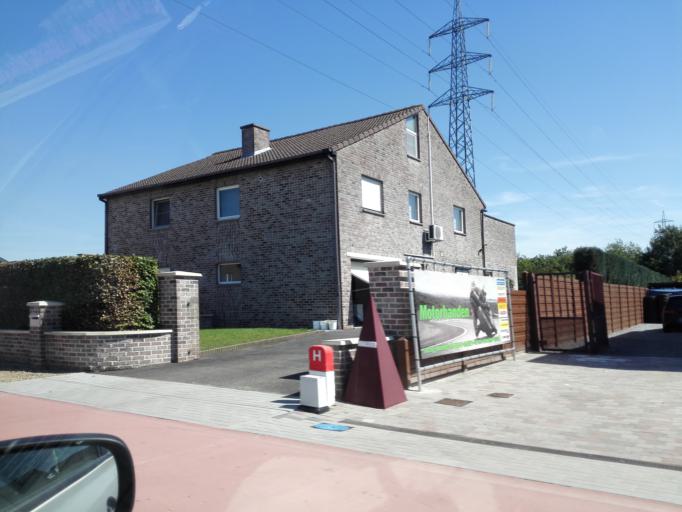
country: BE
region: Flanders
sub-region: Provincie Limburg
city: Opglabbeek
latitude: 51.0348
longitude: 5.5548
